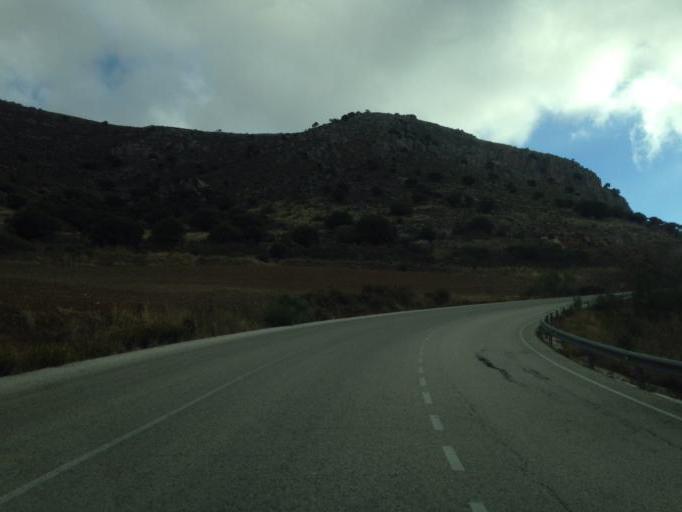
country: ES
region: Andalusia
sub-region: Provincia de Malaga
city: Casabermeja
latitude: 36.9563
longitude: -4.4394
